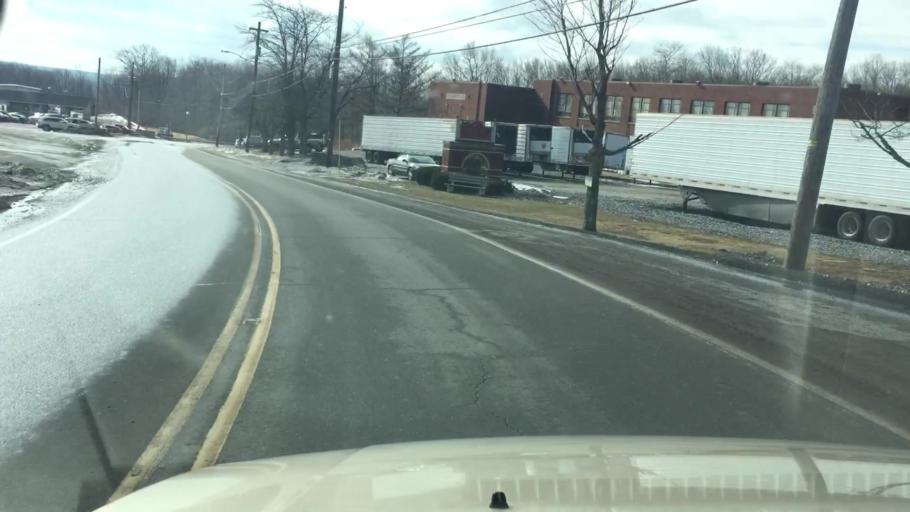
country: US
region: Pennsylvania
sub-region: Luzerne County
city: Freeland
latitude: 41.0113
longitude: -75.8989
